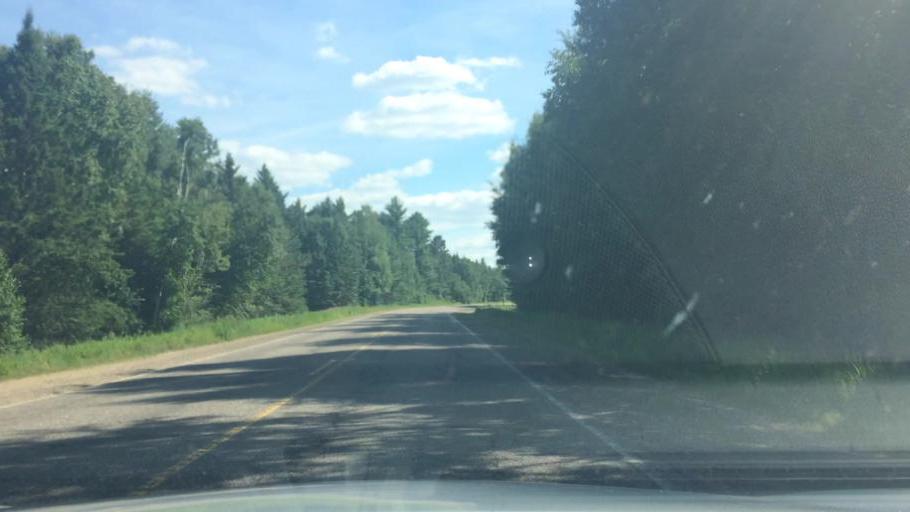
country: US
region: Wisconsin
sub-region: Vilas County
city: Lac du Flambeau
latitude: 46.0659
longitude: -89.6450
